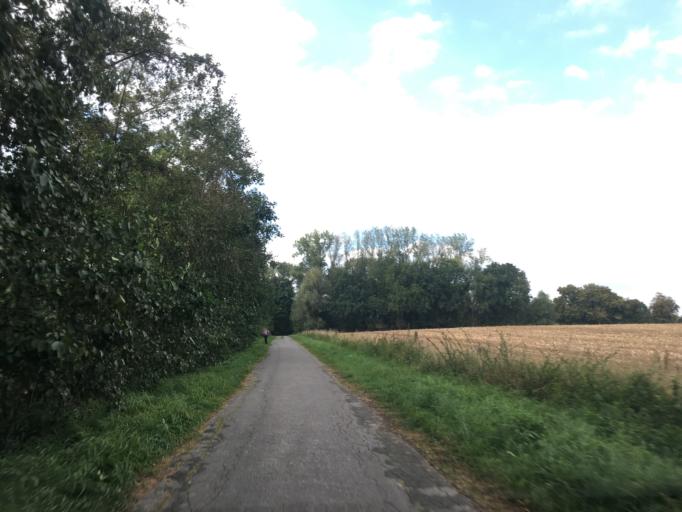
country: DE
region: North Rhine-Westphalia
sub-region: Regierungsbezirk Munster
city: Altenberge
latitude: 51.9824
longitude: 7.5197
